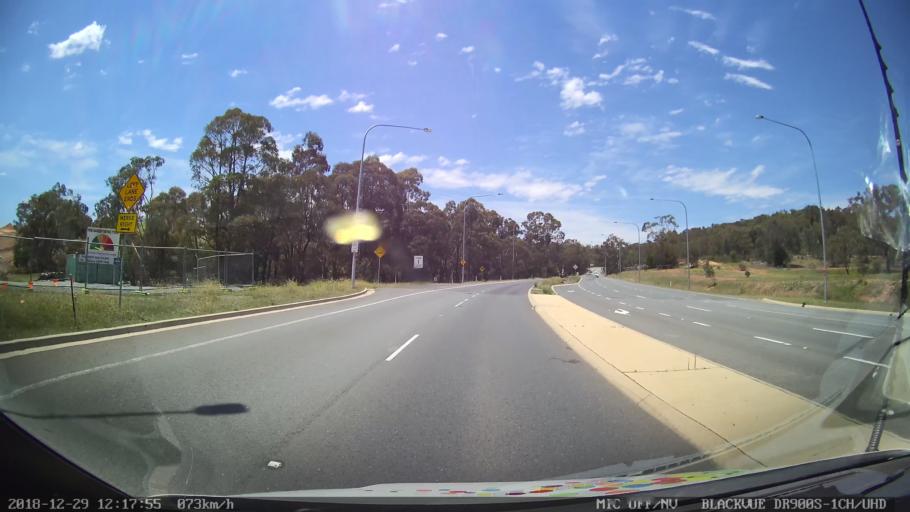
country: AU
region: New South Wales
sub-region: Queanbeyan
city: Queanbeyan
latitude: -35.3790
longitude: 149.2364
